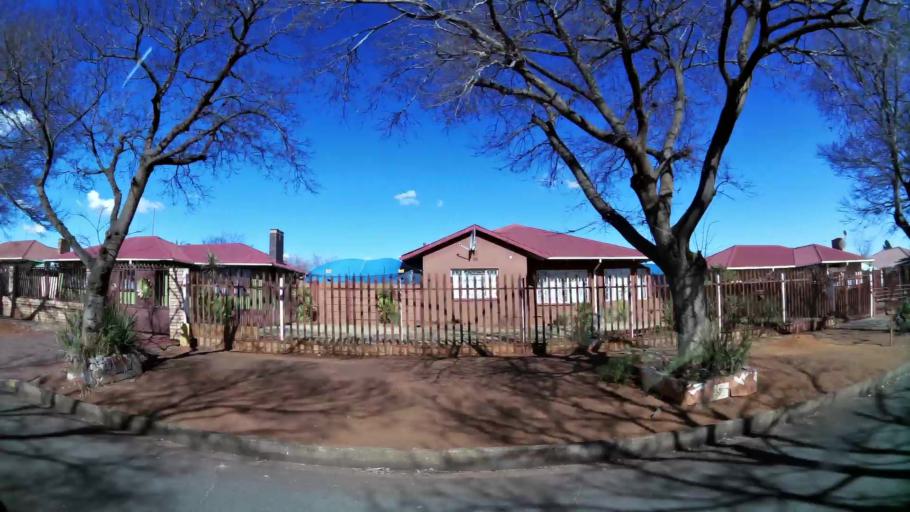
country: ZA
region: Gauteng
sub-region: West Rand District Municipality
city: Carletonville
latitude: -26.3572
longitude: 27.3871
